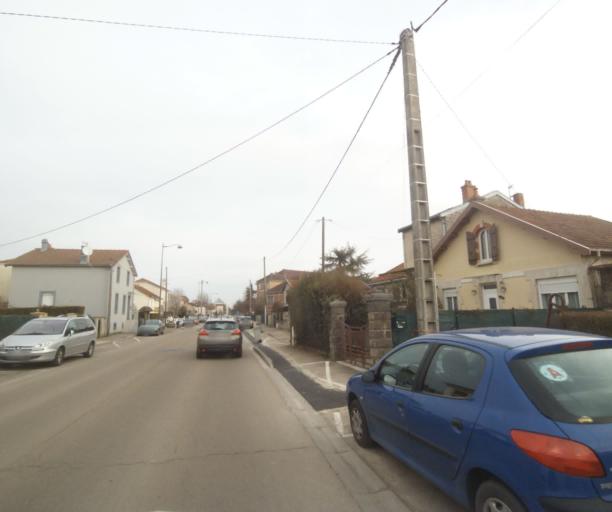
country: FR
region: Champagne-Ardenne
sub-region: Departement de la Haute-Marne
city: Bettancourt-la-Ferree
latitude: 48.6416
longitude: 4.9617
